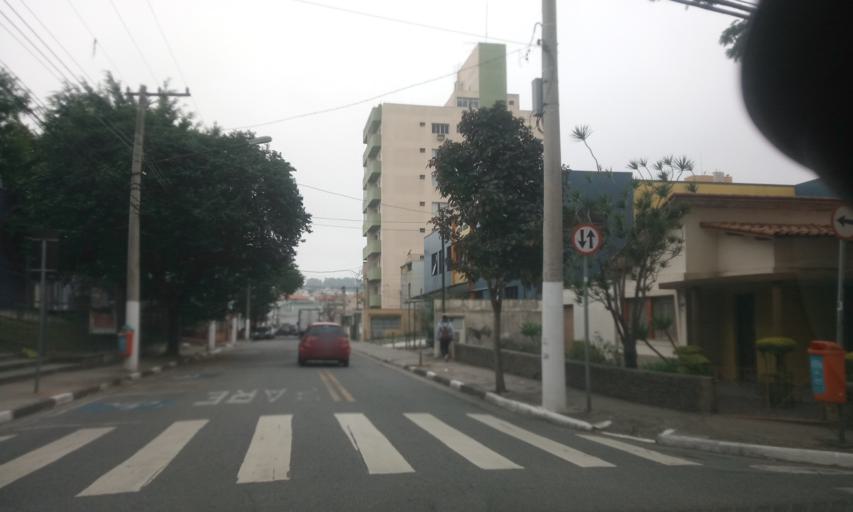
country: BR
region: Sao Paulo
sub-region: Santo Andre
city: Santo Andre
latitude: -23.6533
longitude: -46.5705
